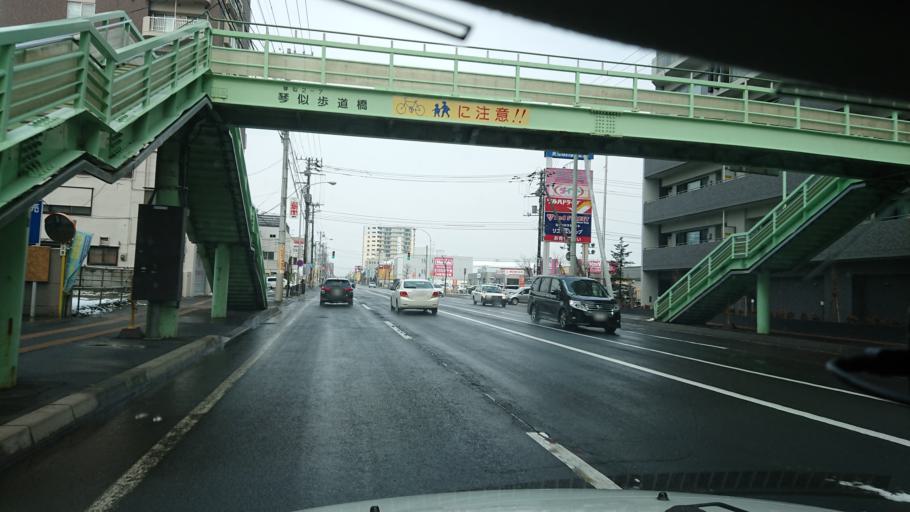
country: JP
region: Hokkaido
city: Sapporo
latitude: 43.0735
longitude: 141.2984
